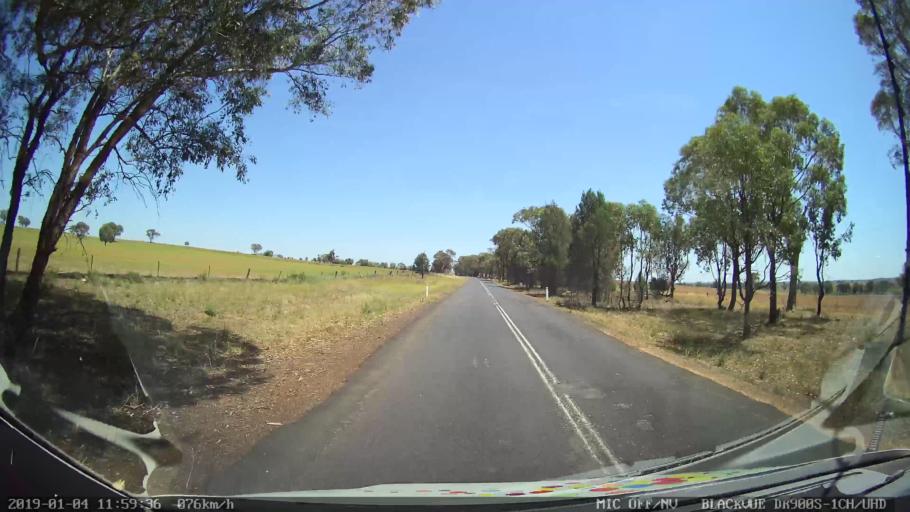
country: AU
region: New South Wales
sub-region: Cabonne
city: Molong
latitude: -32.8119
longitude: 148.6953
